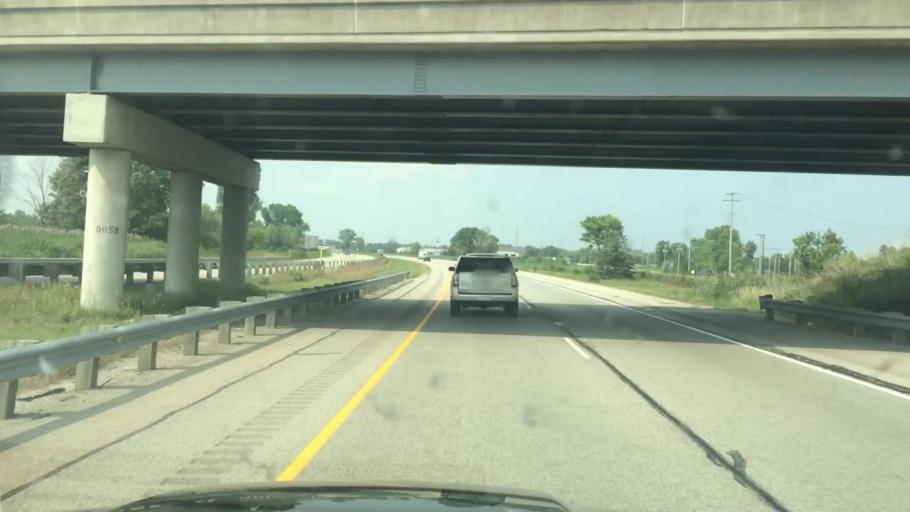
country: US
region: Wisconsin
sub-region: Fond du Lac County
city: North Fond du Lac
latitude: 43.7914
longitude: -88.4831
